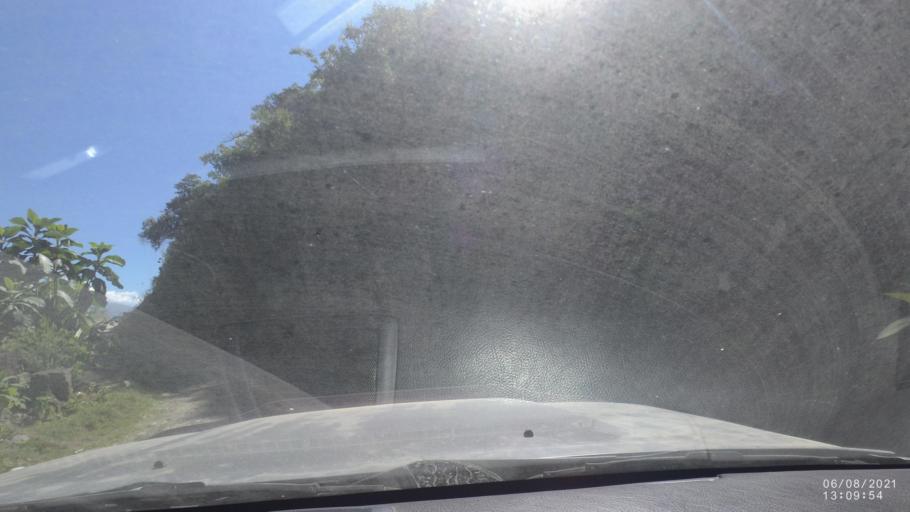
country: BO
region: La Paz
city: Quime
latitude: -16.7261
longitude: -66.7034
